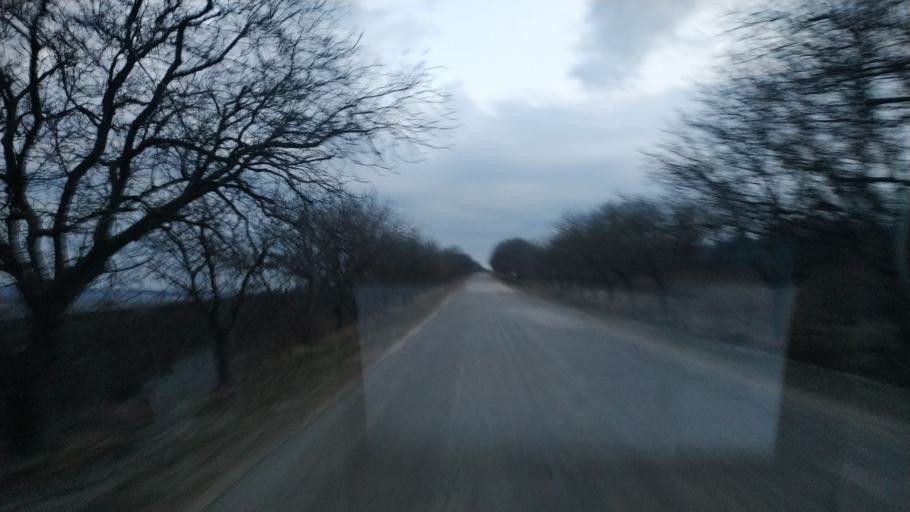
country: MD
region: Anenii Noi
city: Anenii Noi
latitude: 46.9391
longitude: 29.2849
